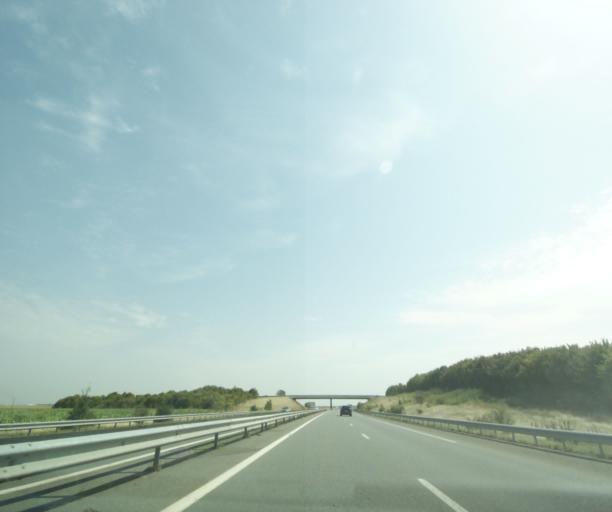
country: FR
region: Pays de la Loire
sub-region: Departement de la Vendee
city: Fontenay-le-Comte
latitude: 46.4311
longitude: -0.8035
